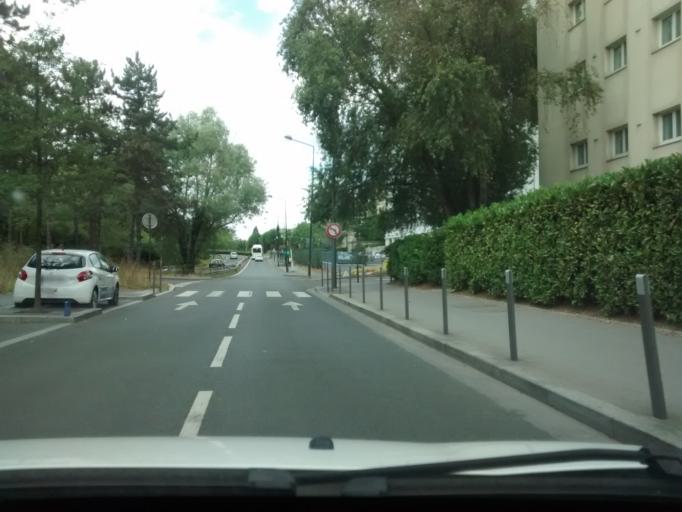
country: FR
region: Ile-de-France
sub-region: Departement de l'Essonne
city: Bievres
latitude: 48.7847
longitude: 2.2248
